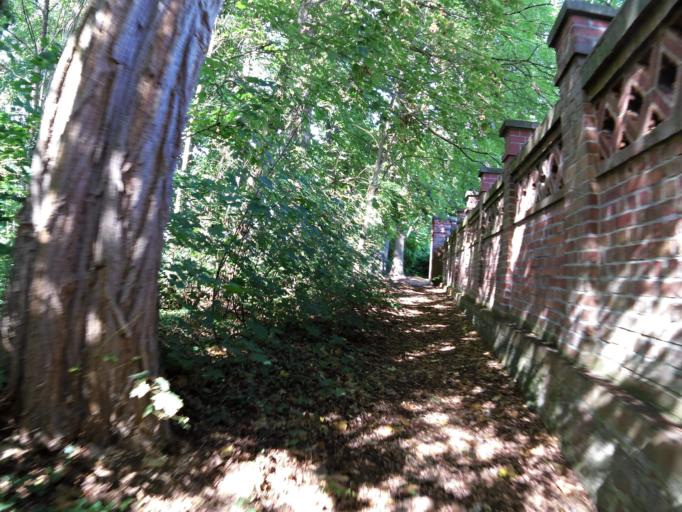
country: DE
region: Brandenburg
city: Storkow
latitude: 52.2614
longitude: 13.9411
